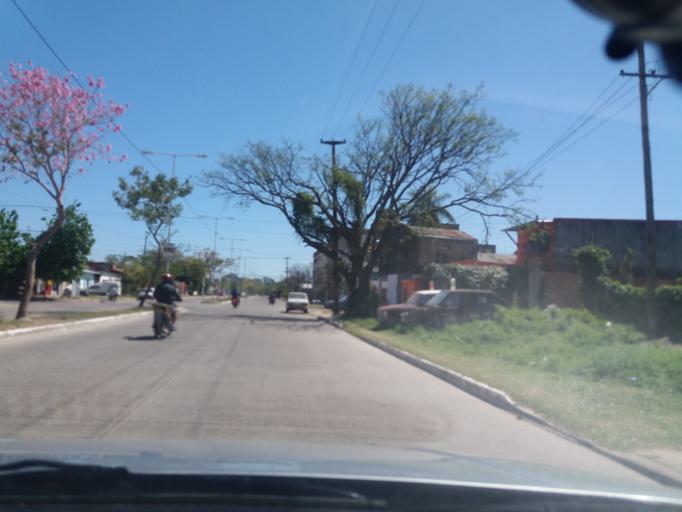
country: AR
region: Corrientes
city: Corrientes
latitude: -27.4884
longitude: -58.8429
